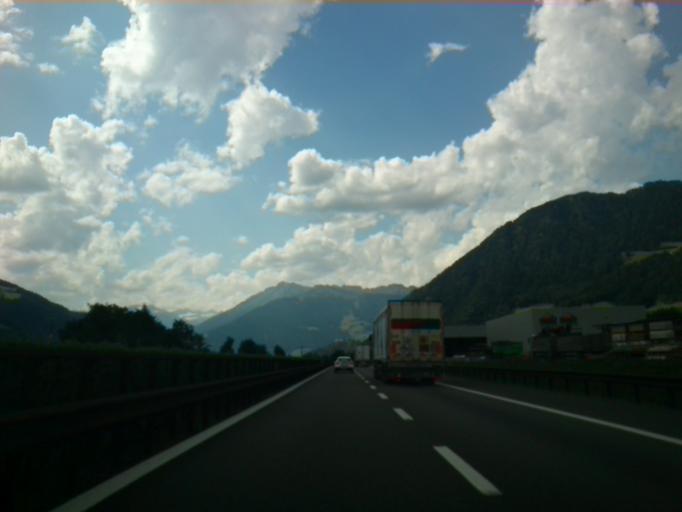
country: IT
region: Trentino-Alto Adige
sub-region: Bolzano
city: Campo di Trens
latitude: 46.8648
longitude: 11.4946
